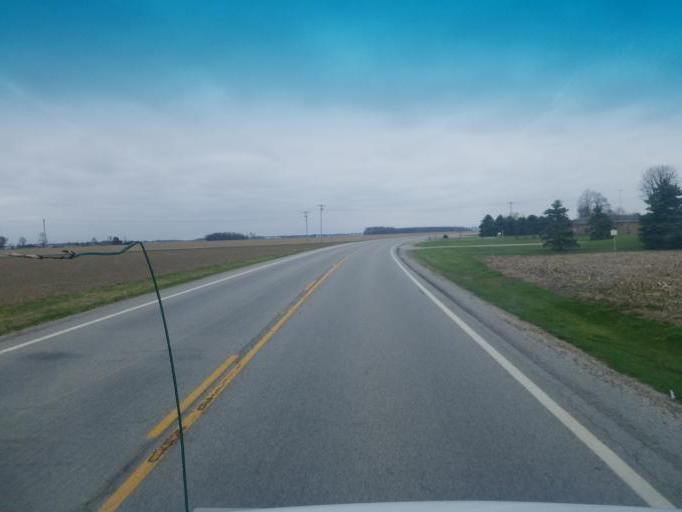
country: US
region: Ohio
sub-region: Van Wert County
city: Van Wert
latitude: 40.9188
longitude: -84.5469
